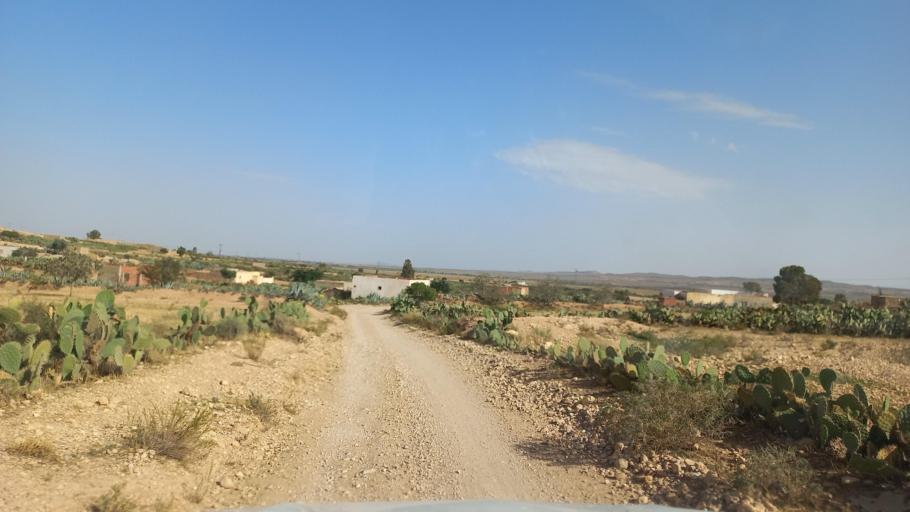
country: TN
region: Al Qasrayn
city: Kasserine
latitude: 35.2562
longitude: 8.9271
